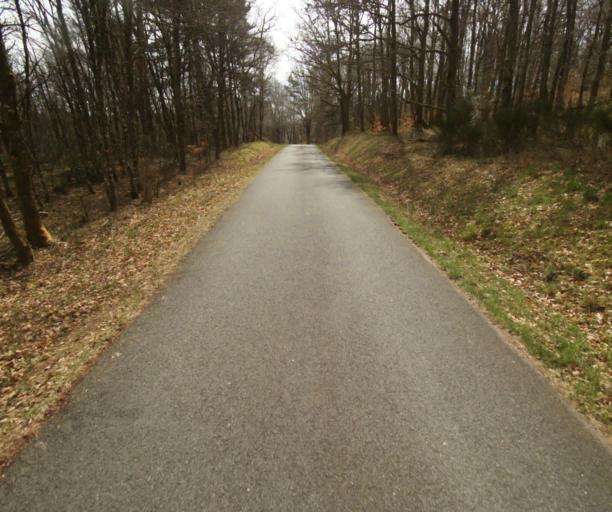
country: FR
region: Limousin
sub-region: Departement de la Correze
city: Egletons
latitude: 45.3719
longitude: 1.9673
